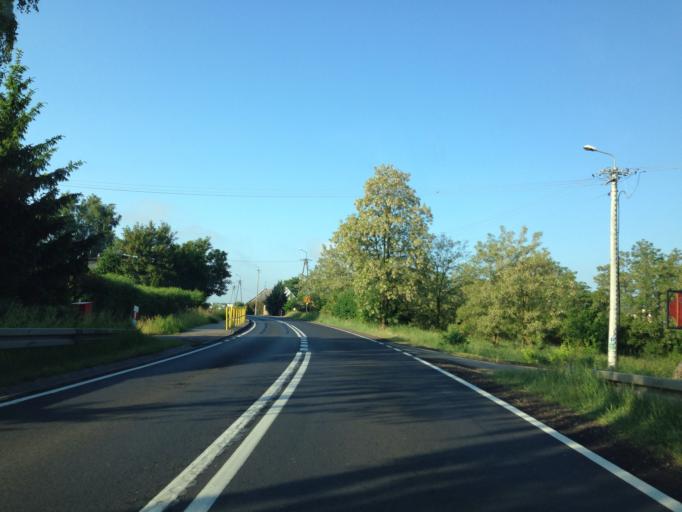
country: PL
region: Kujawsko-Pomorskie
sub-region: Grudziadz
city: Grudziadz
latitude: 53.5251
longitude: 18.8116
